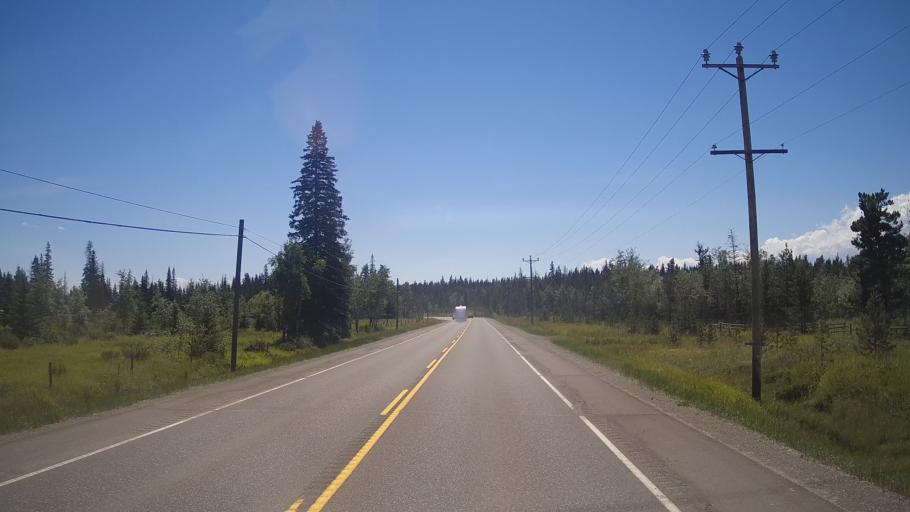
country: CA
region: British Columbia
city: Cache Creek
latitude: 51.2010
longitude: -121.5354
